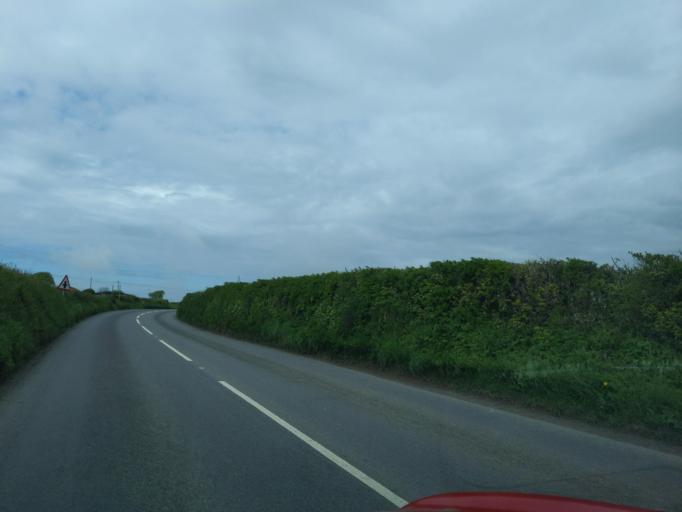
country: GB
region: England
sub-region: Cornwall
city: Wadebridge
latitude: 50.5568
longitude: -4.8633
